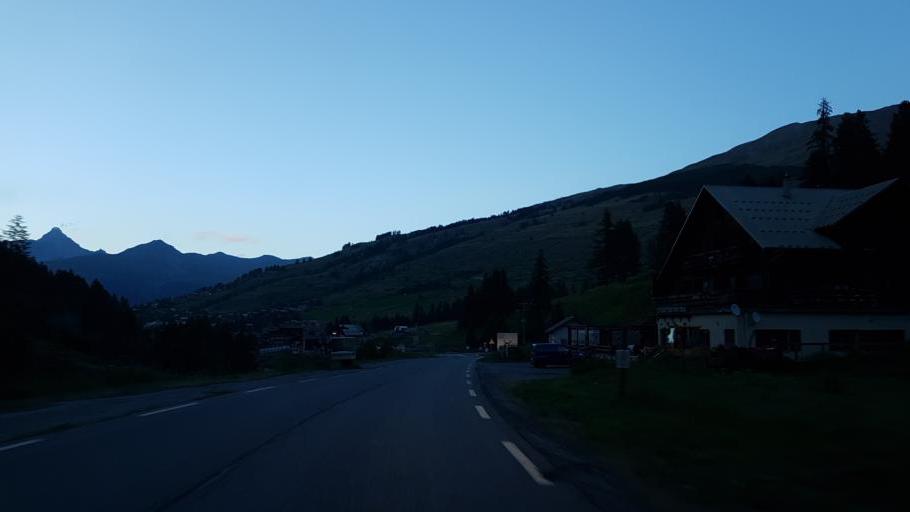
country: IT
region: Piedmont
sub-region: Provincia di Cuneo
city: Pontechianale
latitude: 44.7165
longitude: 6.8477
